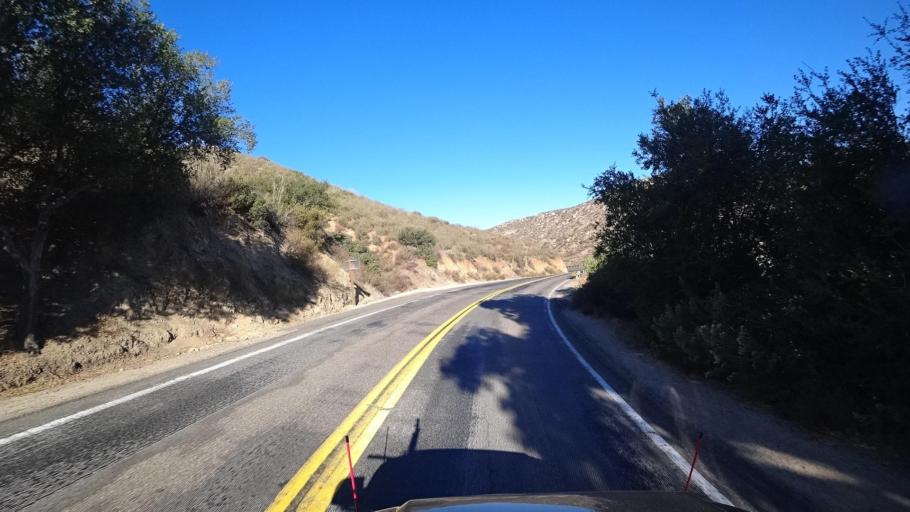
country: MX
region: Baja California
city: Tecate
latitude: 32.5935
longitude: -116.6663
